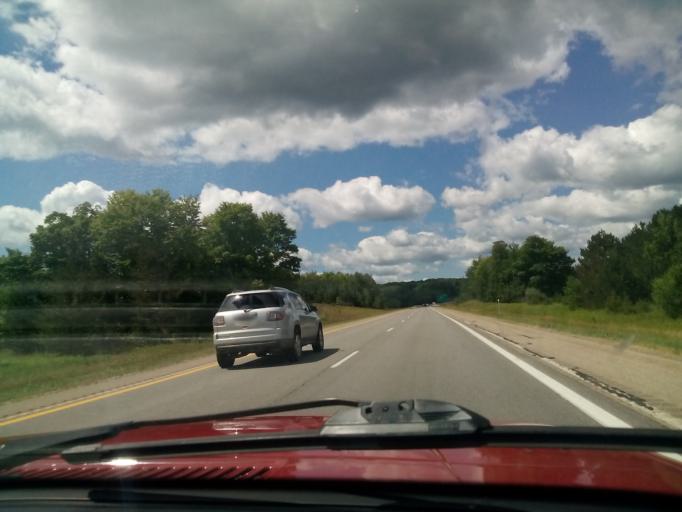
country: US
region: Michigan
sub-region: Ogemaw County
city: West Branch
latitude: 44.2598
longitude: -84.2550
